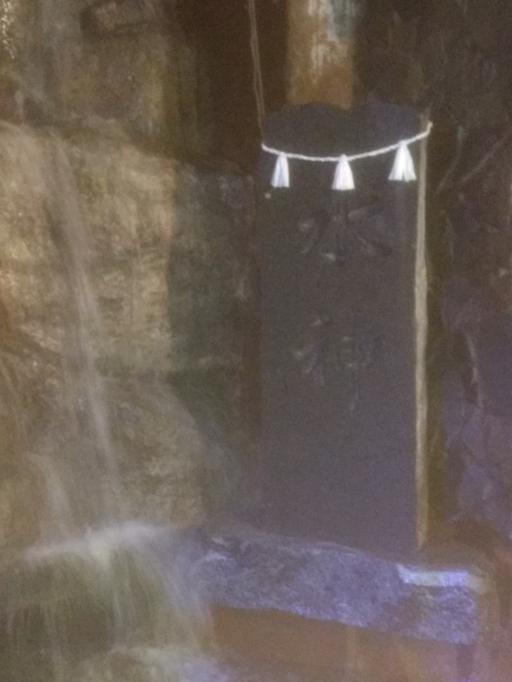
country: JP
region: Kumamoto
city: Aso
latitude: 32.8211
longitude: 131.0997
